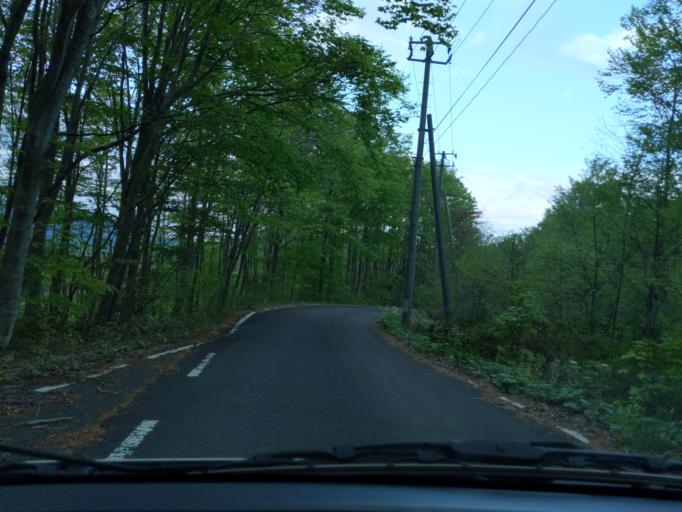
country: JP
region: Iwate
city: Ichinoseki
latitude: 38.9043
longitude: 140.8350
